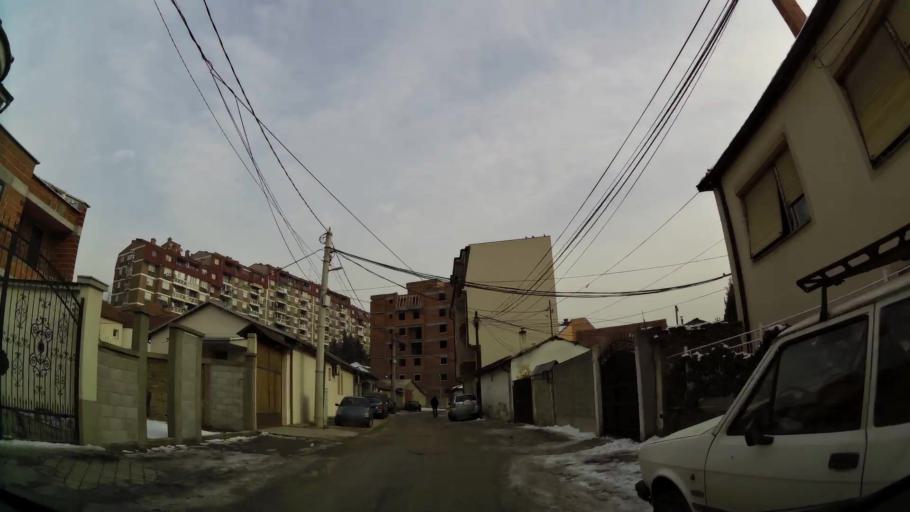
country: MK
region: Cair
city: Cair
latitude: 42.0119
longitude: 21.4343
